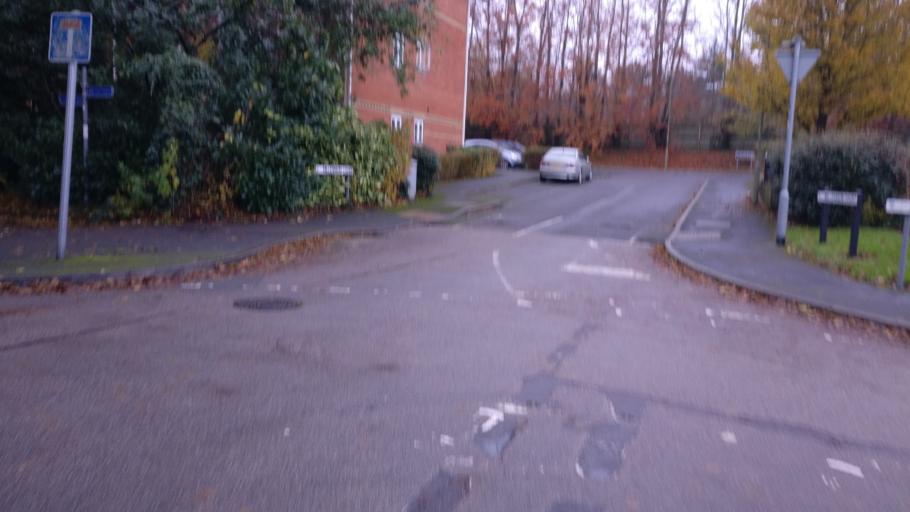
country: GB
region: England
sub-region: Hampshire
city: Basingstoke
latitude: 51.2655
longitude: -1.1023
